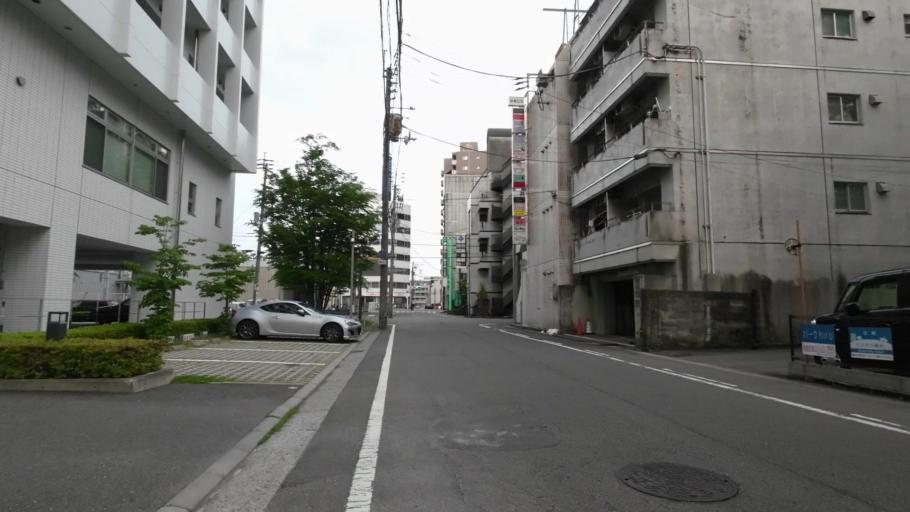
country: JP
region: Kochi
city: Kochi-shi
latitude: 33.5632
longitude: 133.5422
